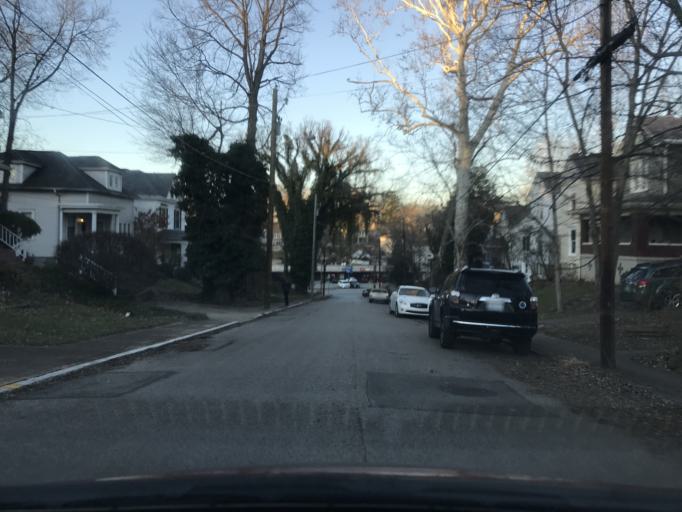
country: US
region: Indiana
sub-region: Clark County
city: Jeffersonville
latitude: 38.2586
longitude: -85.7087
